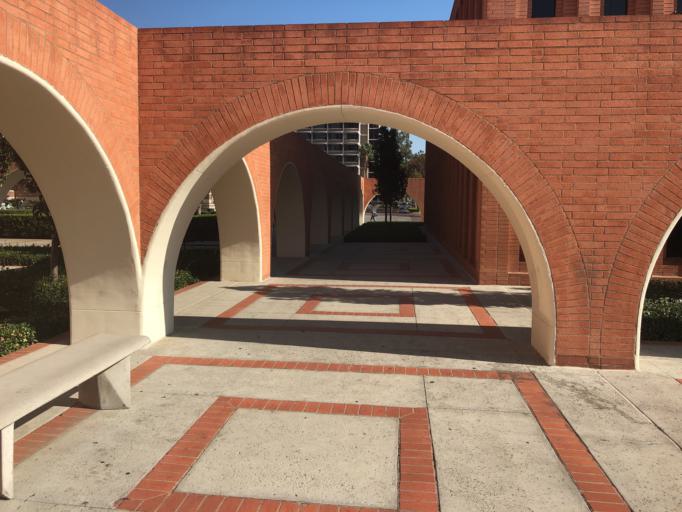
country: US
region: California
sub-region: Los Angeles County
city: Los Angeles
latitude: 34.0218
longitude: -118.2839
